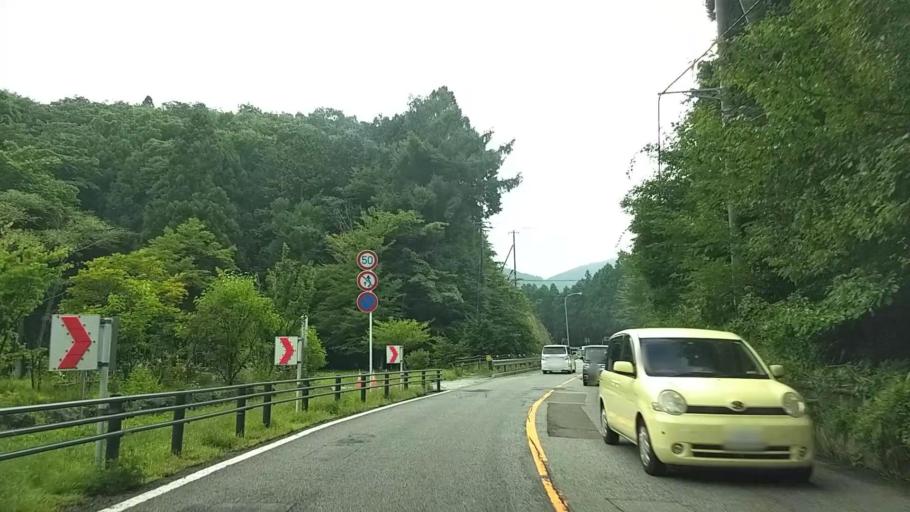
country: JP
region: Yamanashi
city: Fujikawaguchiko
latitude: 35.4582
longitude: 138.6094
